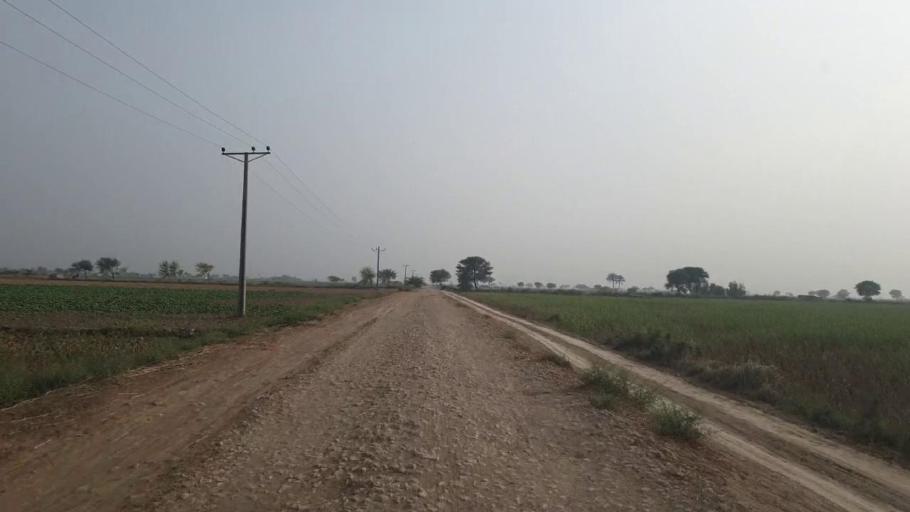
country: PK
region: Sindh
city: Mirpur Batoro
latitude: 24.5664
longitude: 68.4188
